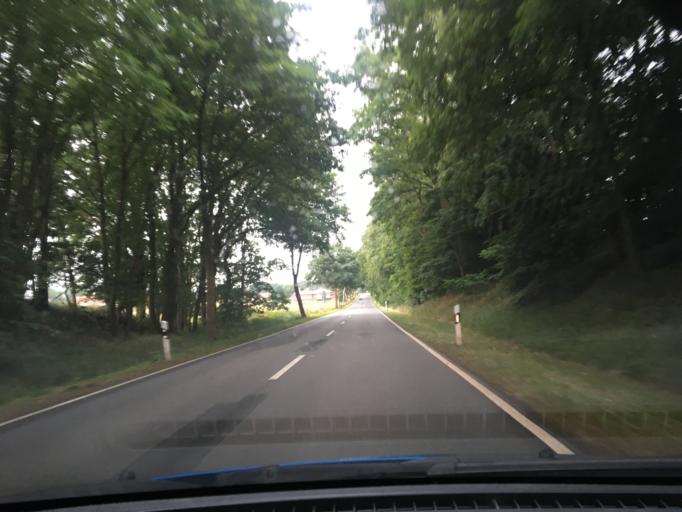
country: DE
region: Lower Saxony
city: Egestorf
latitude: 53.2015
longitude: 10.0671
